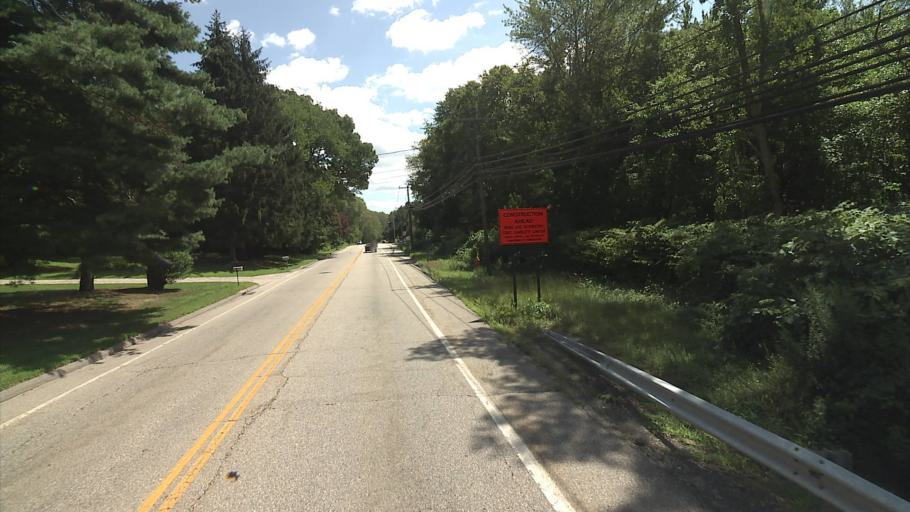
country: US
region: Connecticut
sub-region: New London County
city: Central Waterford
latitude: 41.3515
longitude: -72.1571
